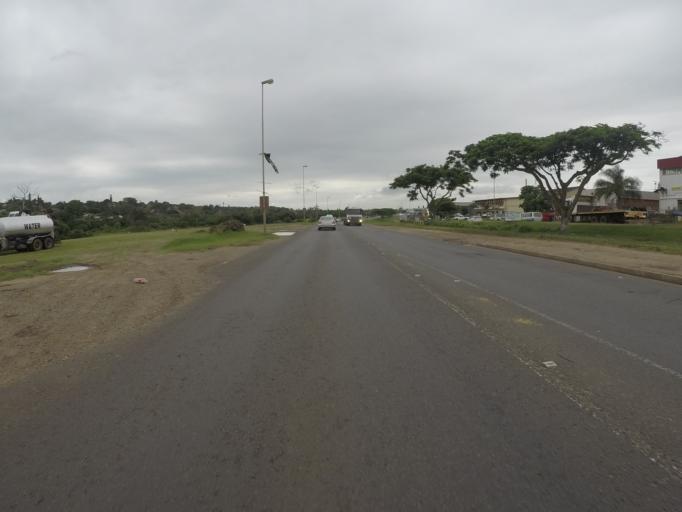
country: ZA
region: KwaZulu-Natal
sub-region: uThungulu District Municipality
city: Empangeni
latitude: -28.7730
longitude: 31.9016
